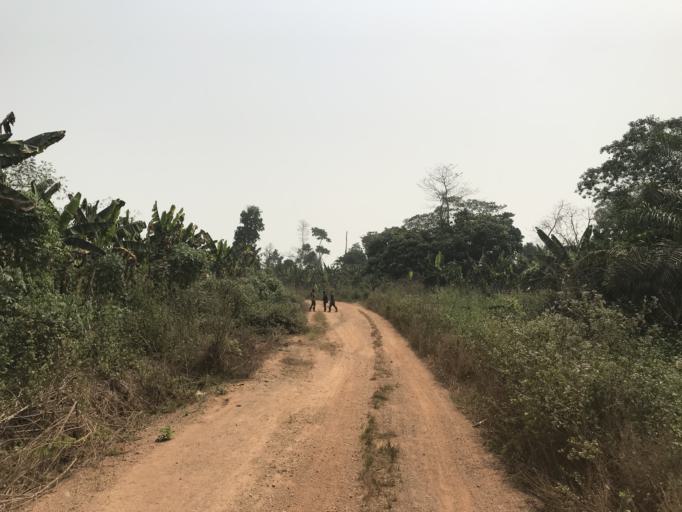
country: NG
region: Osun
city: Ifetedo
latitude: 7.0513
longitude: 4.4744
